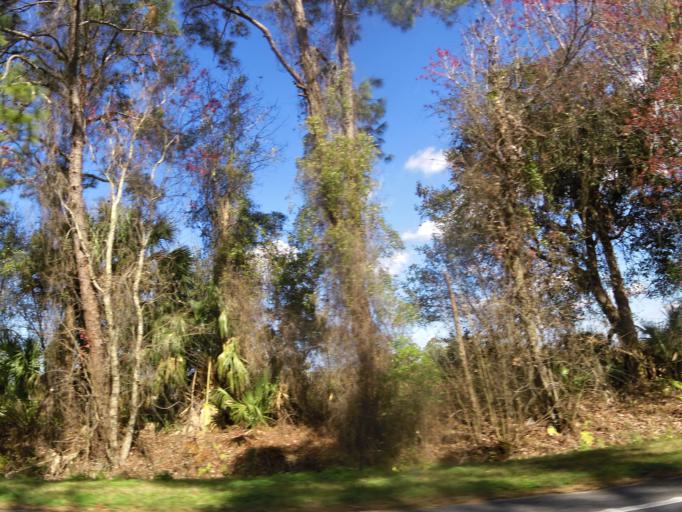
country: US
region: Florida
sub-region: Volusia County
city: De Leon Springs
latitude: 29.1500
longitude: -81.3735
